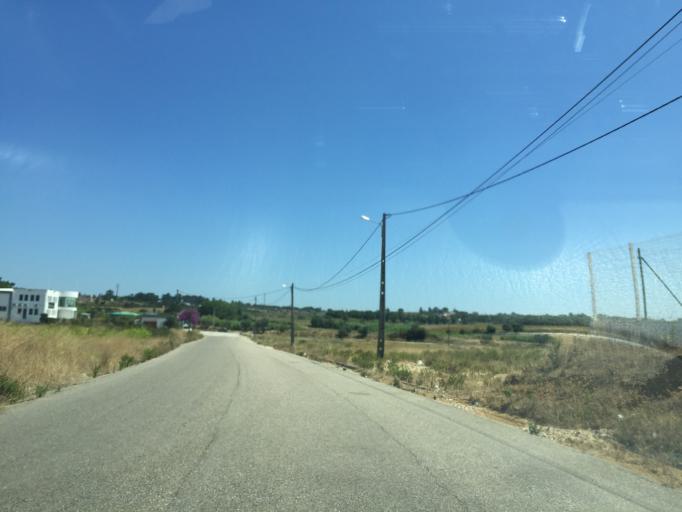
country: PT
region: Lisbon
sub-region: Azambuja
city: Aveiras de Cima
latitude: 39.1476
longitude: -8.8992
